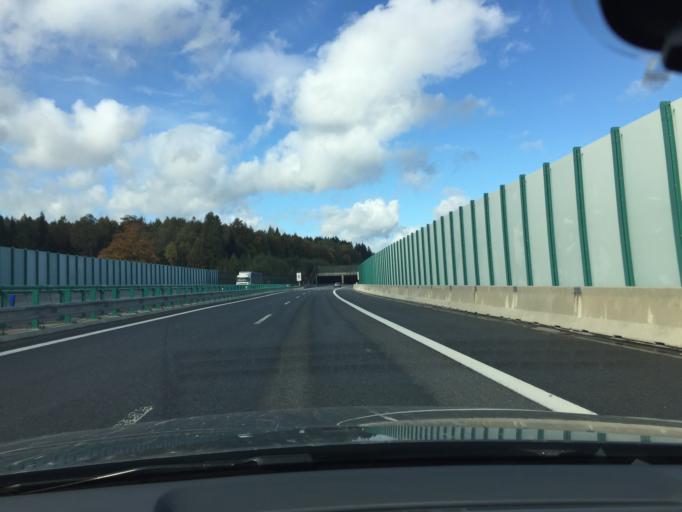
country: DE
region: Saxony
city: Liebstadt
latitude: 50.7834
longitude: 13.8980
